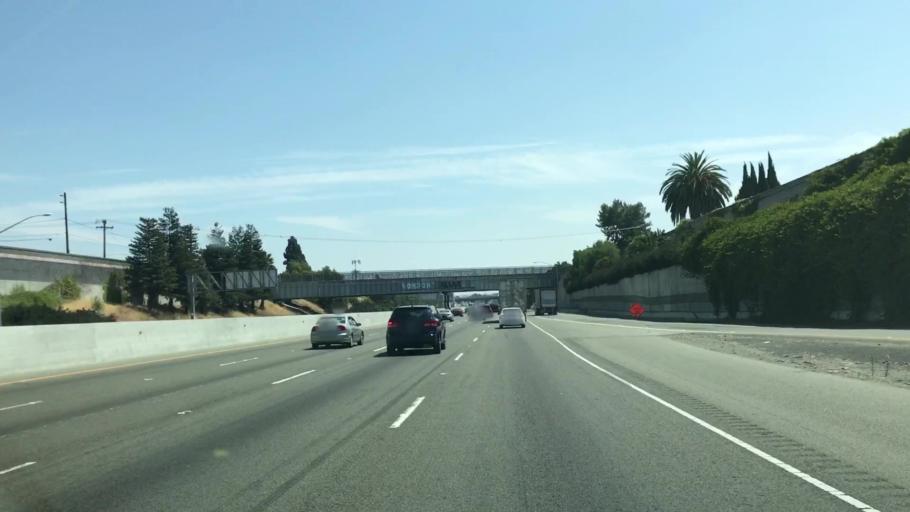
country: US
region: California
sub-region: Alameda County
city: Newark
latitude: 37.5444
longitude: -122.0214
